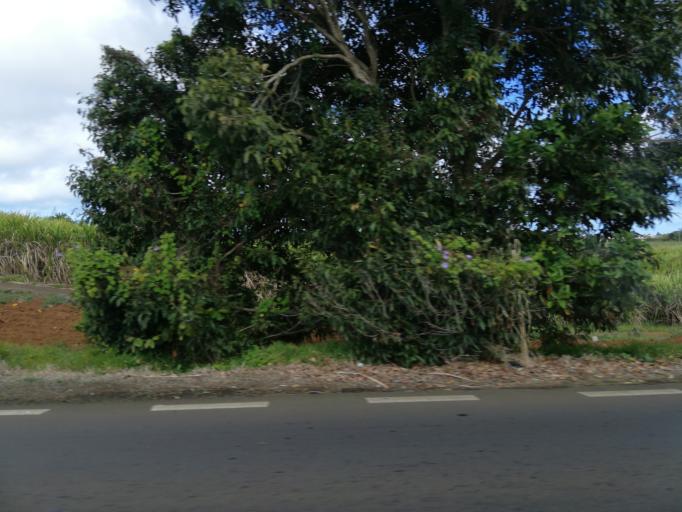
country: MU
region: Grand Port
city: Plaine Magnien
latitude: -20.4164
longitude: 57.6721
